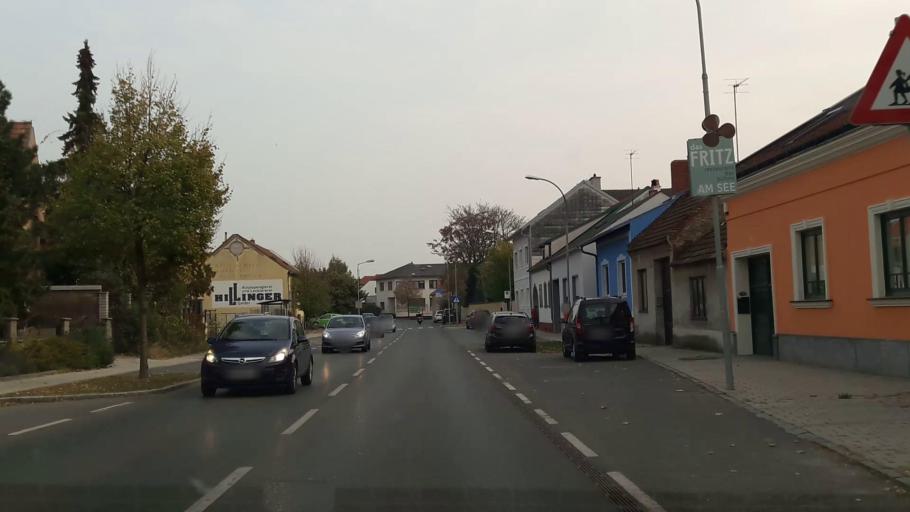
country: AT
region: Burgenland
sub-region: Politischer Bezirk Neusiedl am See
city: Weiden am See
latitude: 47.9311
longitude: 16.8629
